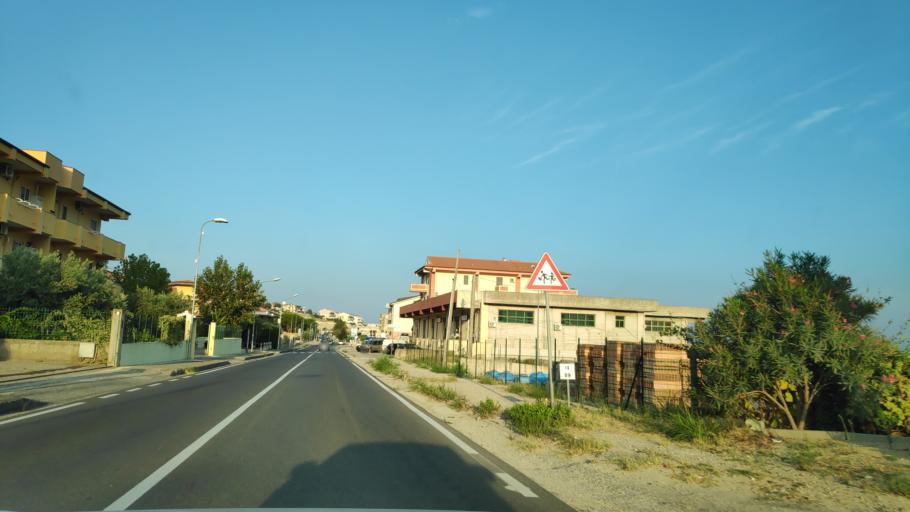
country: IT
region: Calabria
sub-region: Provincia di Catanzaro
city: Martelli-Laganosa
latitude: 38.6792
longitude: 16.5292
